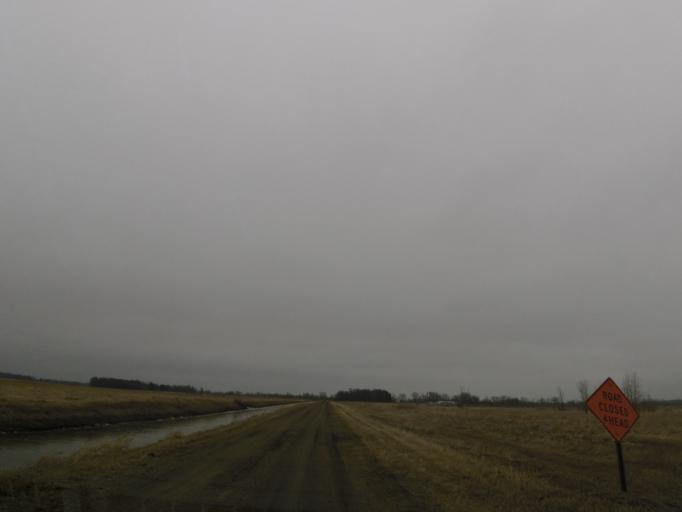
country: US
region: North Dakota
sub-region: Walsh County
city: Grafton
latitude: 48.3686
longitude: -97.1669
